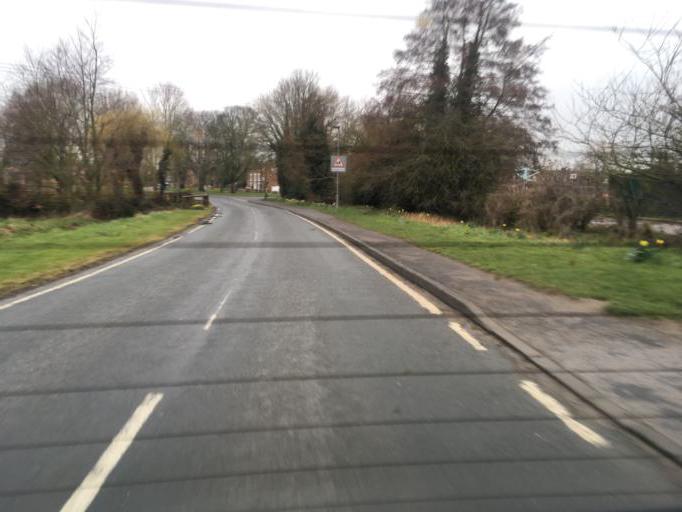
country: GB
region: England
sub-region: City of York
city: Holtby
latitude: 53.9623
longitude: -0.9758
